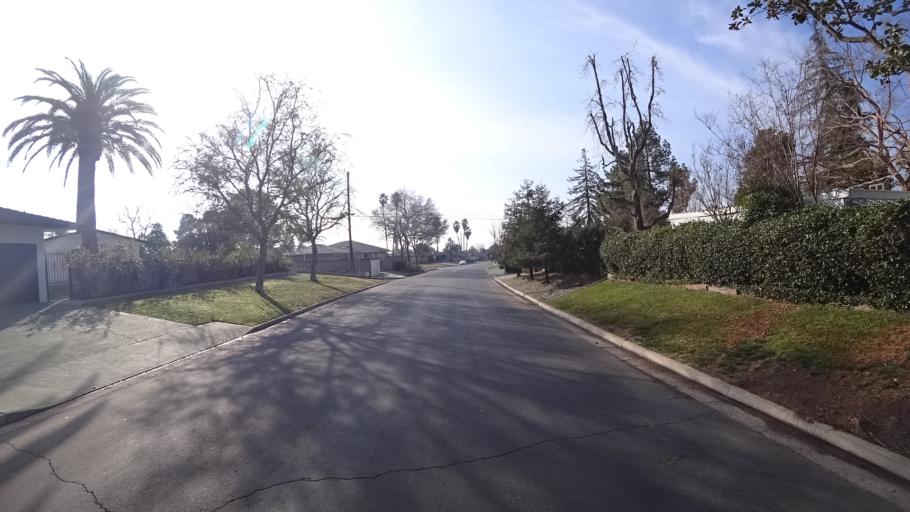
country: US
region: California
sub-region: Kern County
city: Oildale
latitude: 35.4082
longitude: -118.9795
